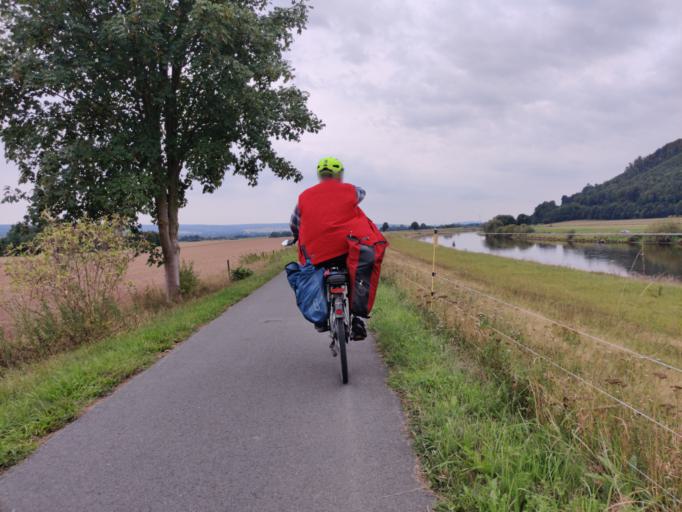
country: DE
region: Lower Saxony
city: Bevern
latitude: 51.8747
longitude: 9.4683
